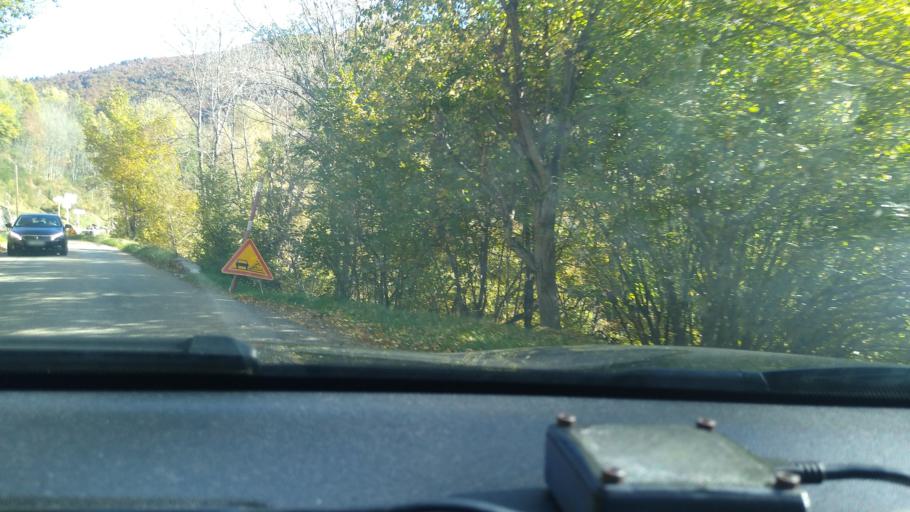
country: FR
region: Midi-Pyrenees
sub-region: Departement de l'Ariege
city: Ax-les-Thermes
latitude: 42.7201
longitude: 1.8680
